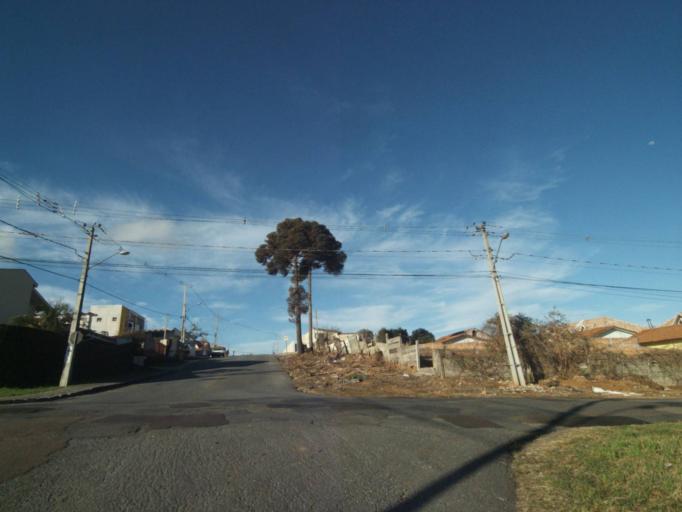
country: BR
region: Parana
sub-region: Curitiba
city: Curitiba
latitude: -25.3857
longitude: -49.2548
